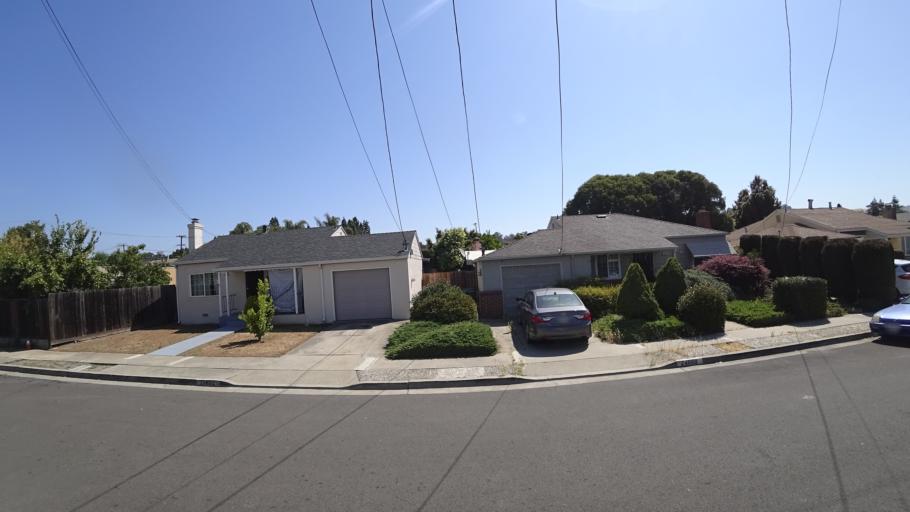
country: US
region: California
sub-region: Alameda County
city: Hayward
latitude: 37.6603
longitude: -122.0793
